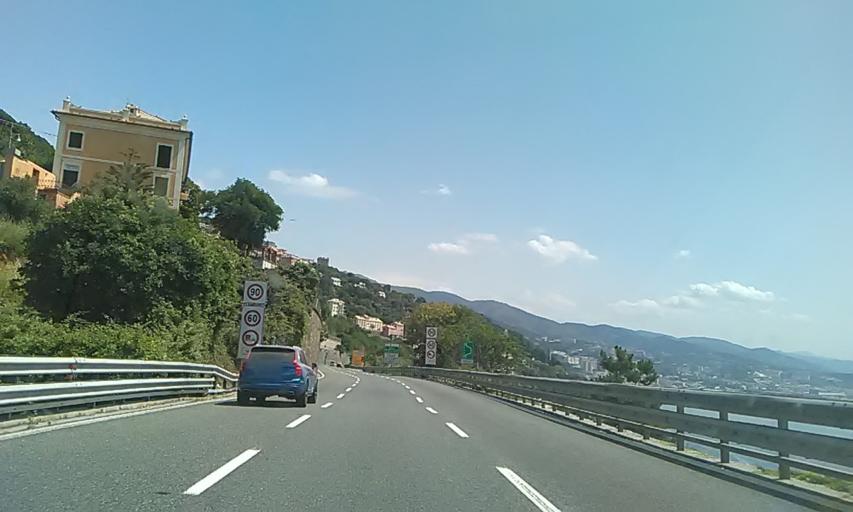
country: IT
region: Liguria
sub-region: Provincia di Genova
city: Mele
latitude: 44.4191
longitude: 8.7254
